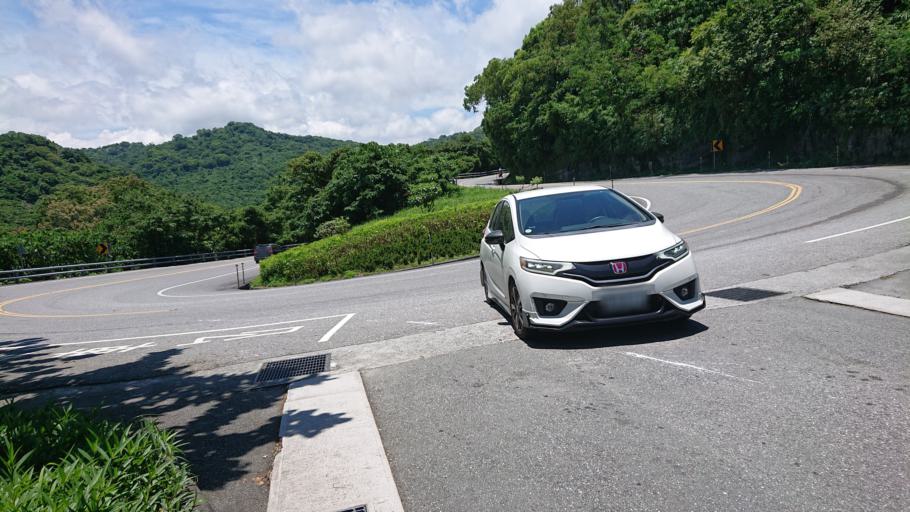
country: TW
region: Taiwan
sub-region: Hualien
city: Hualian
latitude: 23.7317
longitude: 121.5583
